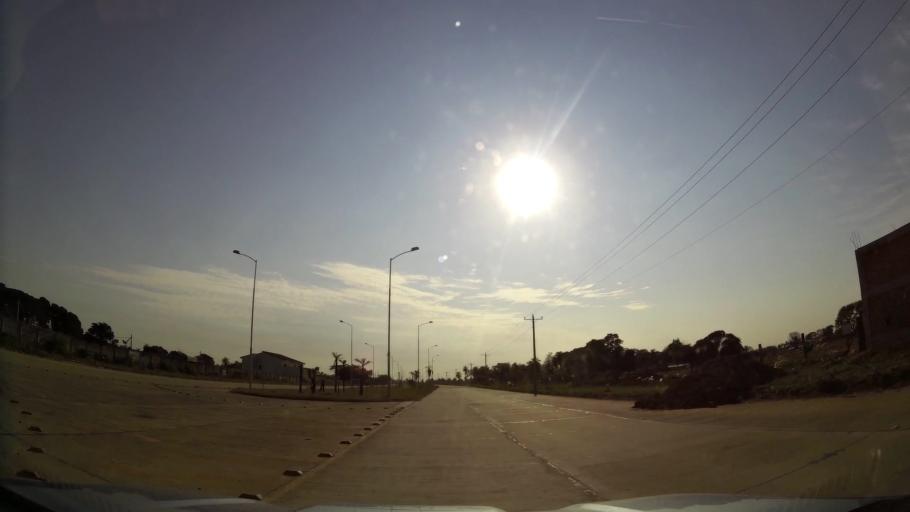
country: BO
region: Santa Cruz
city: Santa Cruz de la Sierra
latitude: -17.6994
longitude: -63.1261
